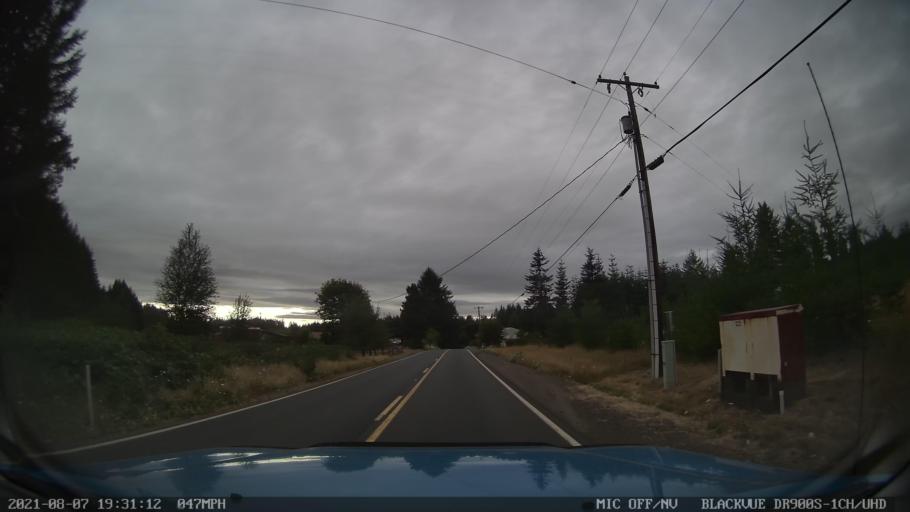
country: US
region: Oregon
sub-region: Linn County
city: Lyons
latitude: 44.8901
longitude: -122.6307
